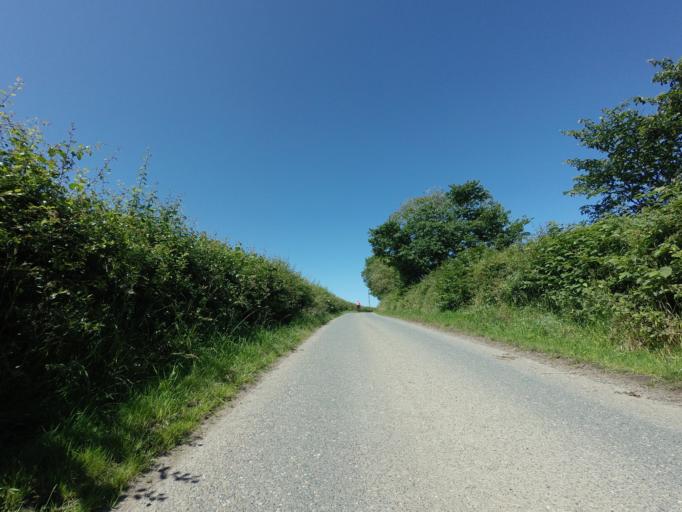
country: GB
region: Scotland
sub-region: Aberdeenshire
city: Macduff
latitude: 57.6333
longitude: -2.4890
